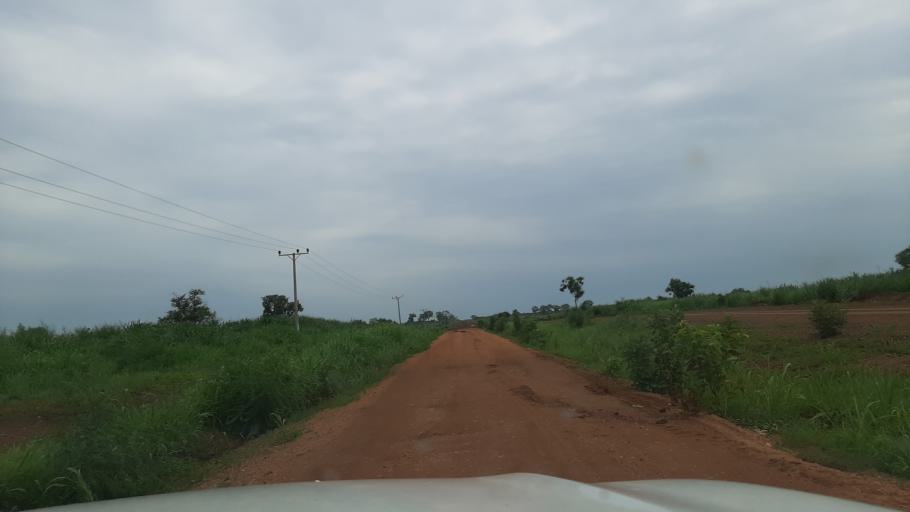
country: ET
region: Gambela
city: Gambela
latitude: 8.1876
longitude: 34.5008
